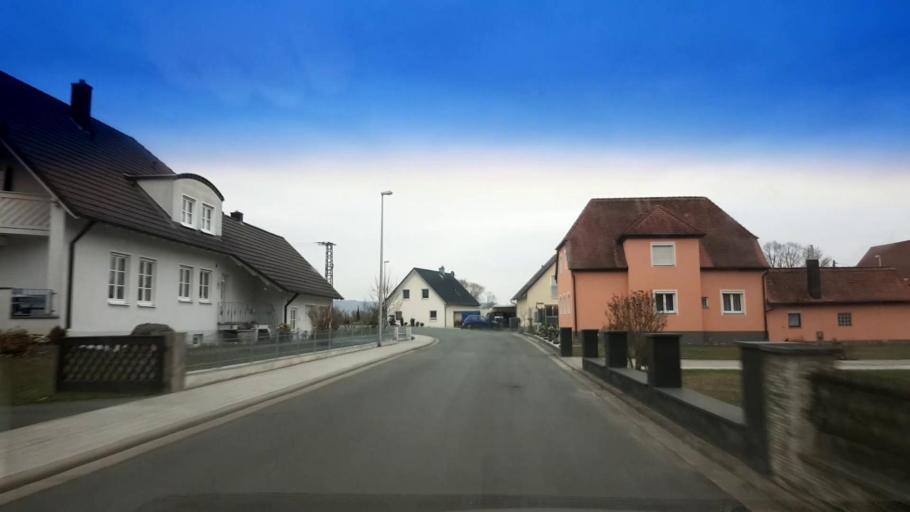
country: DE
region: Bavaria
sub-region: Upper Franconia
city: Altendorf
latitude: 49.7917
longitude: 11.0023
